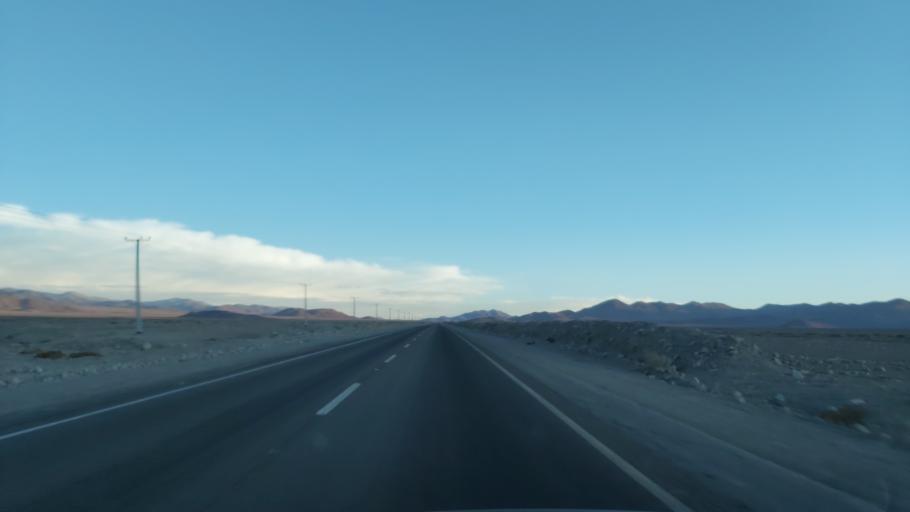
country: CL
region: Atacama
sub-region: Provincia de Chanaral
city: Diego de Almagro
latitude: -26.6881
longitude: -69.9319
